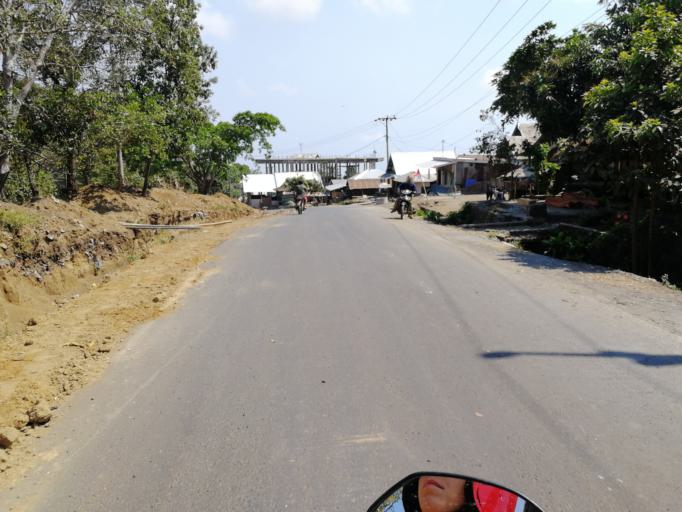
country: ID
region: West Nusa Tenggara
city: Lelongken
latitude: -8.3236
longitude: 116.4962
